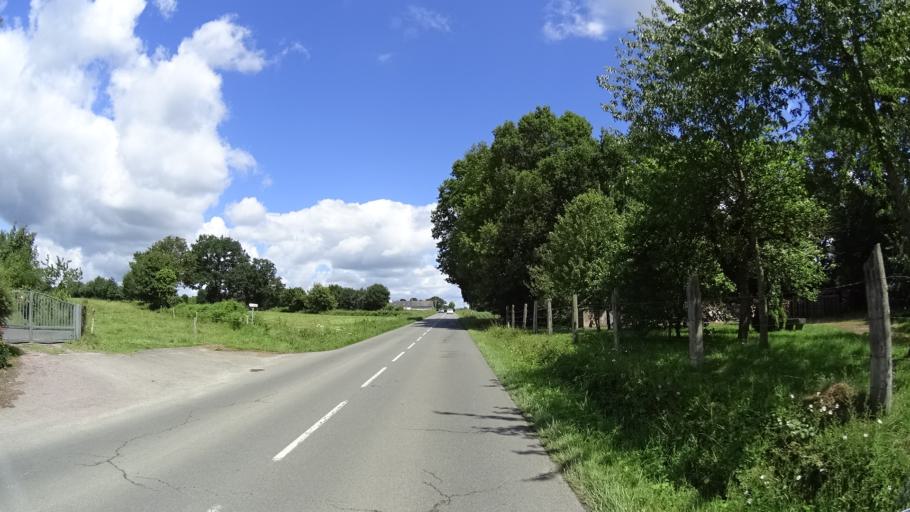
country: FR
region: Brittany
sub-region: Departement d'Ille-et-Vilaine
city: Saint-Gilles
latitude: 48.1384
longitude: -1.8279
